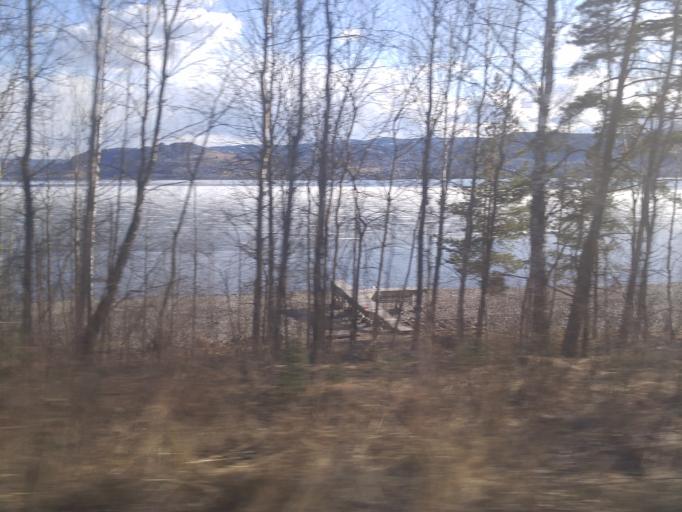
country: NO
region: Hedmark
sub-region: Ringsaker
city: Moelv
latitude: 60.9815
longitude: 10.6459
